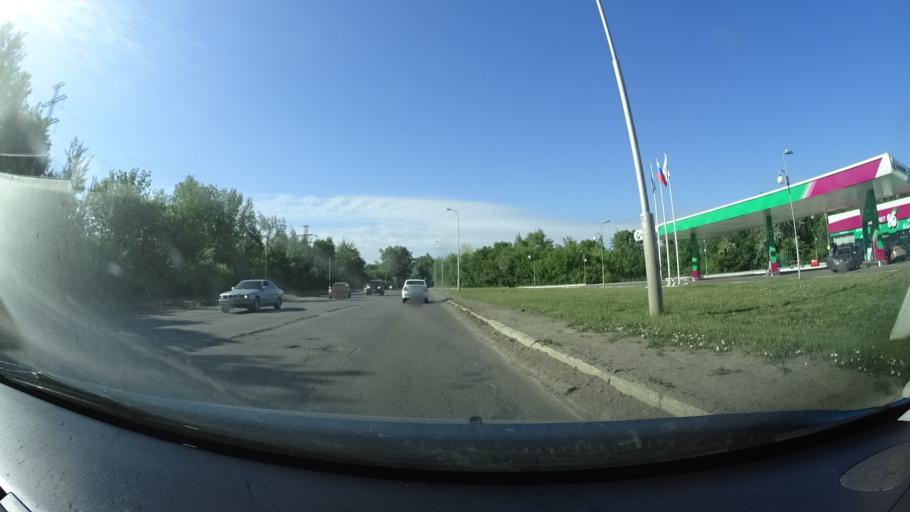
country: RU
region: Bashkortostan
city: Ufa
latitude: 54.8465
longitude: 56.0765
